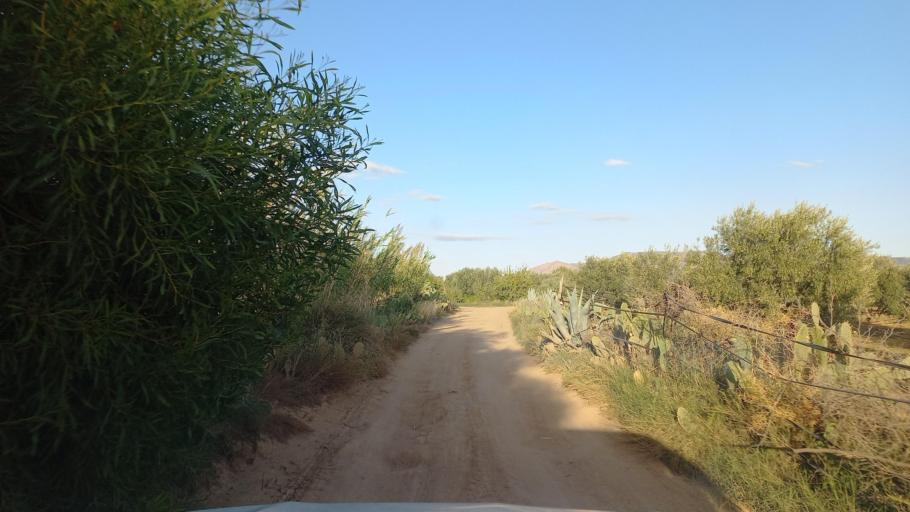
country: TN
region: Al Qasrayn
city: Sbiba
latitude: 35.4196
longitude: 9.1341
